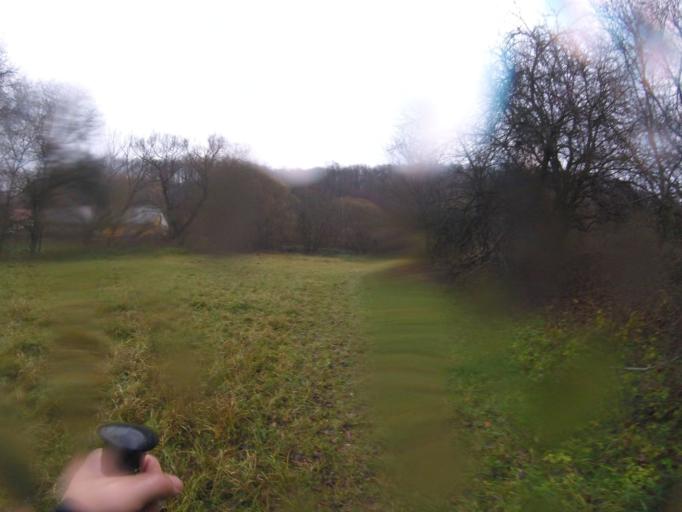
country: HU
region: Pest
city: Szob
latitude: 47.8517
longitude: 18.8491
